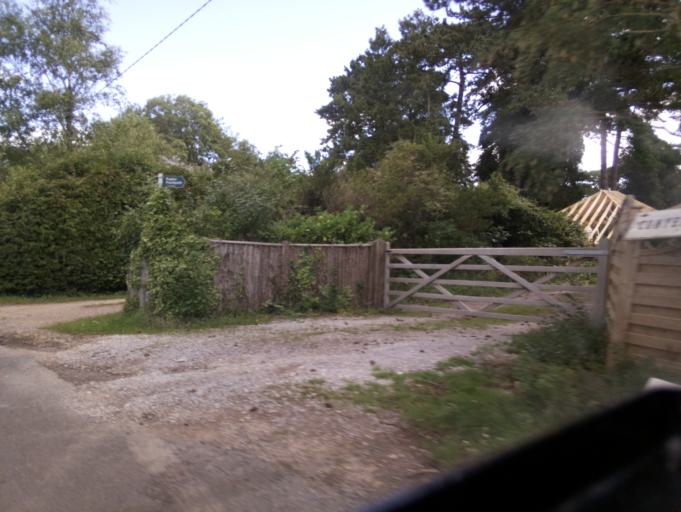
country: GB
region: England
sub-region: Gloucestershire
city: Newent
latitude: 51.8569
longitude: -2.3530
